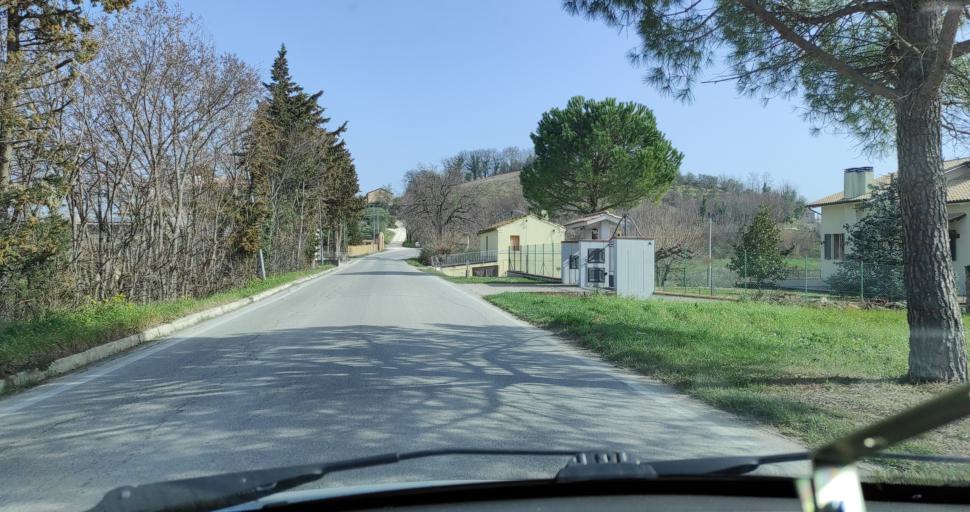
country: IT
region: The Marches
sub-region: Provincia di Macerata
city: Mogliano
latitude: 43.1836
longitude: 13.4598
